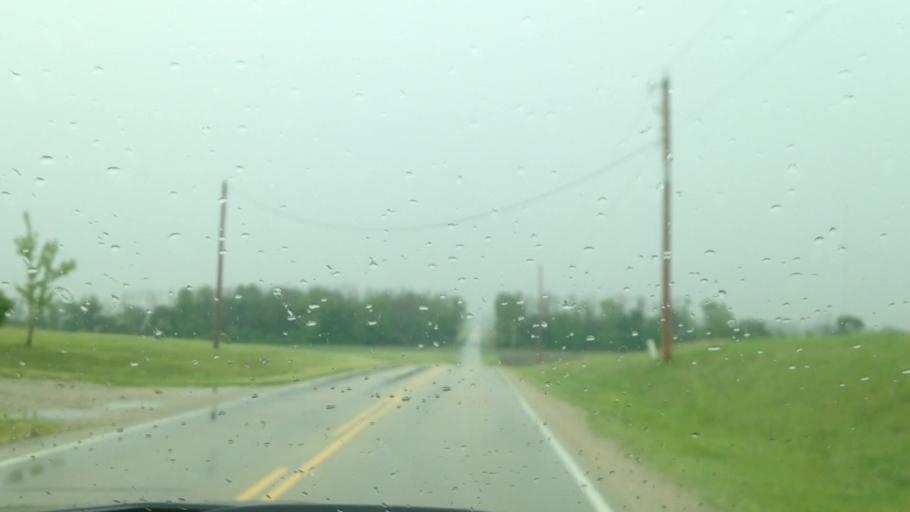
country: US
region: Ohio
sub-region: Darke County
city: Greenville
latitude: 40.1506
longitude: -84.6236
